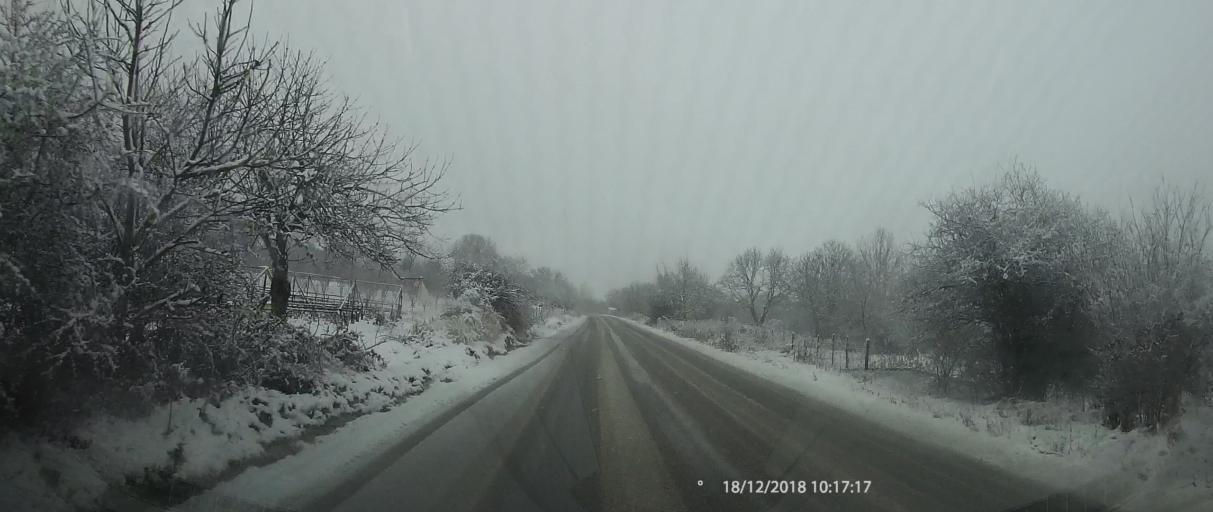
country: GR
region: Thessaly
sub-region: Nomos Larisis
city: Livadi
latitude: 40.1227
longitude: 22.2122
